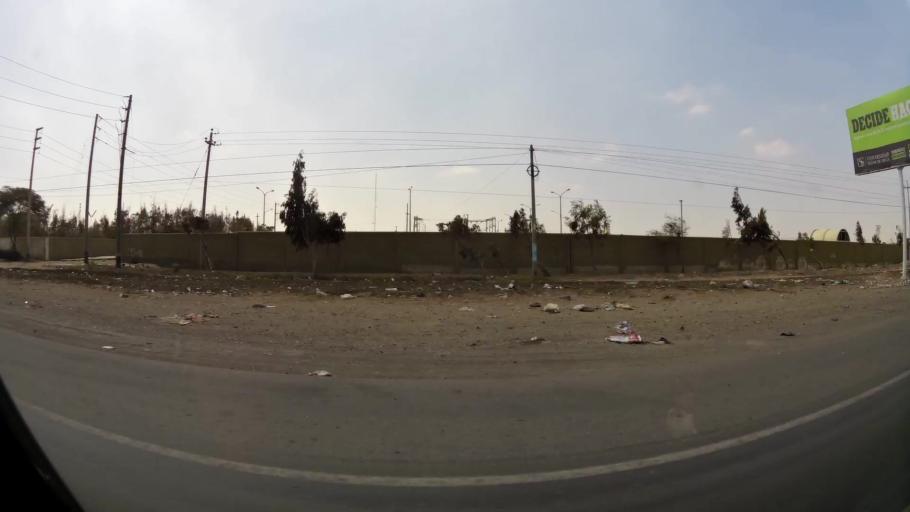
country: PE
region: La Libertad
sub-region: Provincia de Pacasmayo
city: Pacasmayo
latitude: -7.4129
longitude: -79.5517
